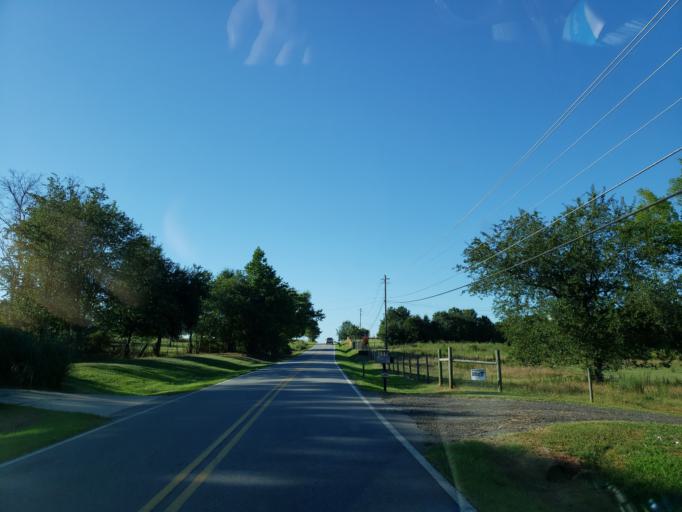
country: US
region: Georgia
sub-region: Bartow County
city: Euharlee
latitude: 34.0988
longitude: -84.9906
